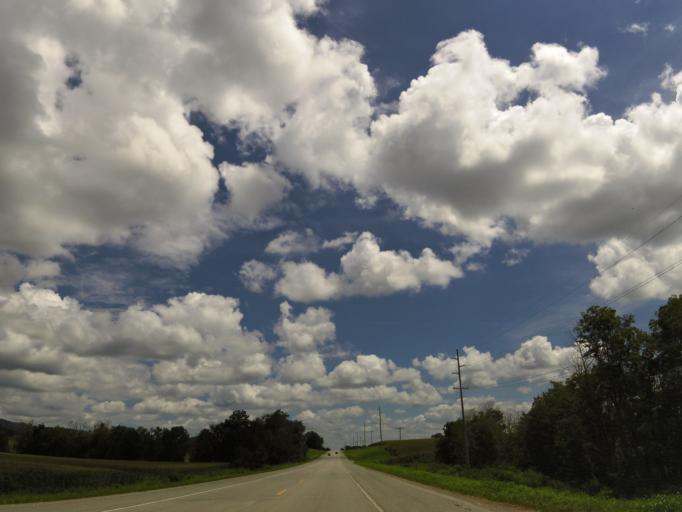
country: US
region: Kentucky
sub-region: Bell County
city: Middlesboro
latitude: 36.5072
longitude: -83.7934
